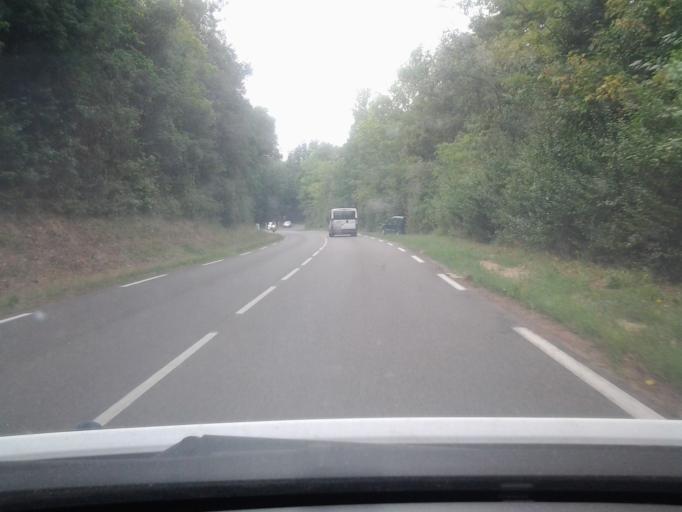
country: FR
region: Pays de la Loire
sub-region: Departement de la Vendee
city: Longeville-sur-Mer
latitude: 46.3908
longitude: -1.4724
